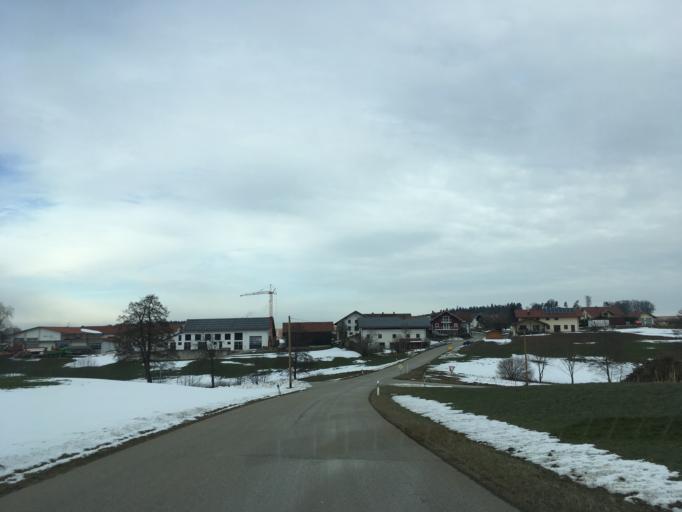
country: DE
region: Bavaria
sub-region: Upper Bavaria
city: Jettenbach
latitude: 48.1245
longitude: 12.3830
